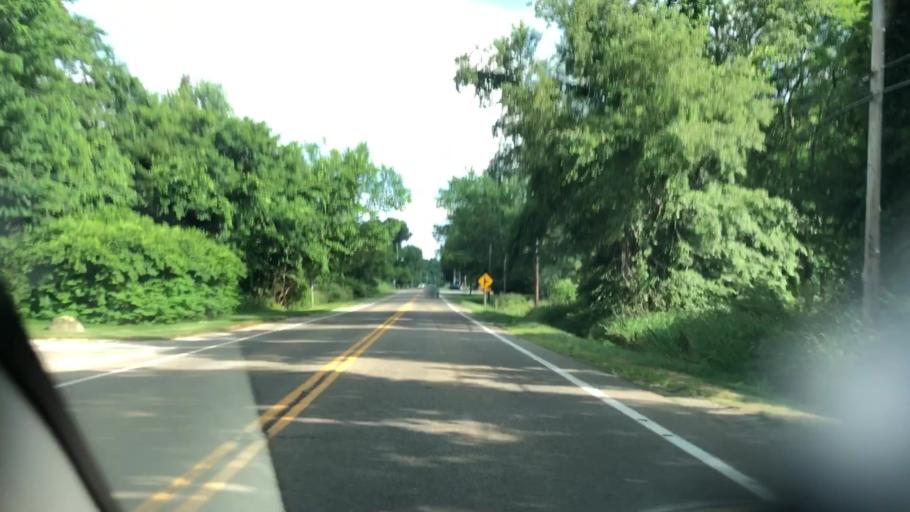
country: US
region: Ohio
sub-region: Summit County
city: Norton
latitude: 41.0832
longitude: -81.6442
